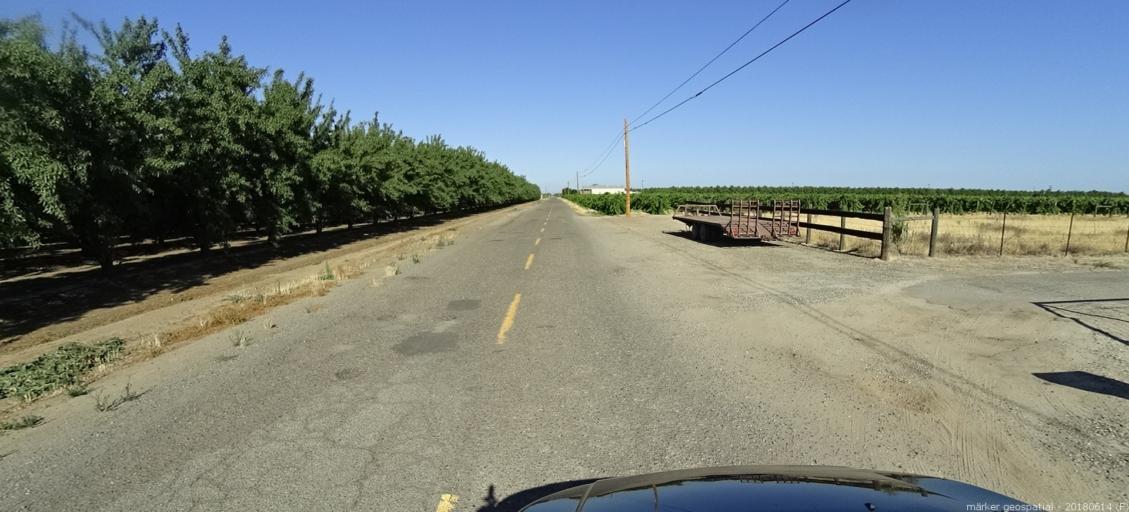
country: US
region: California
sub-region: Madera County
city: Madera
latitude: 36.9311
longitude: -120.1204
